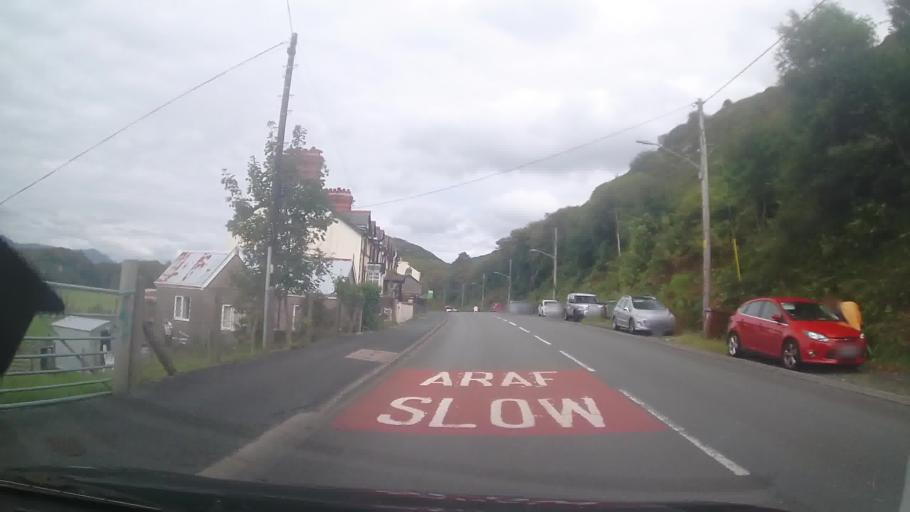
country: GB
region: Wales
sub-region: Gwynedd
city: Barmouth
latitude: 52.6894
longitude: -4.0513
